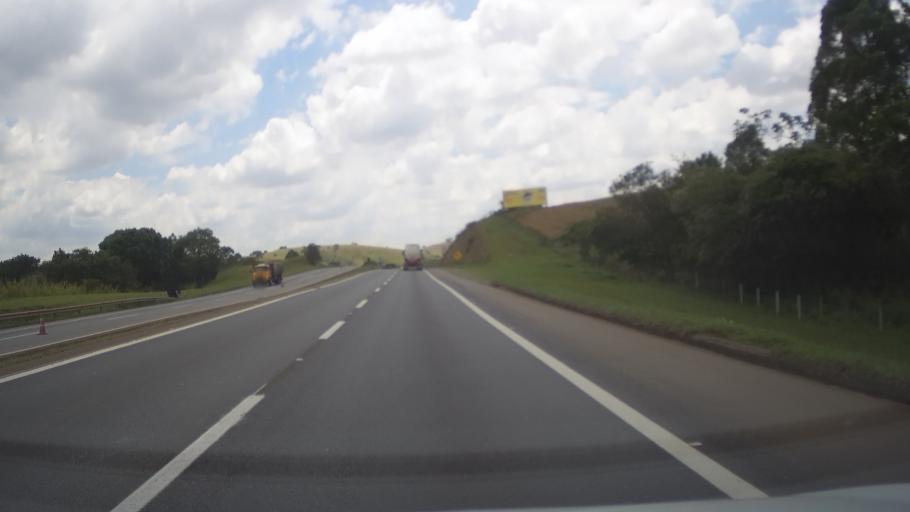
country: BR
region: Minas Gerais
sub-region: Campanha
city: Campanha
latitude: -21.7169
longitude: -45.3774
